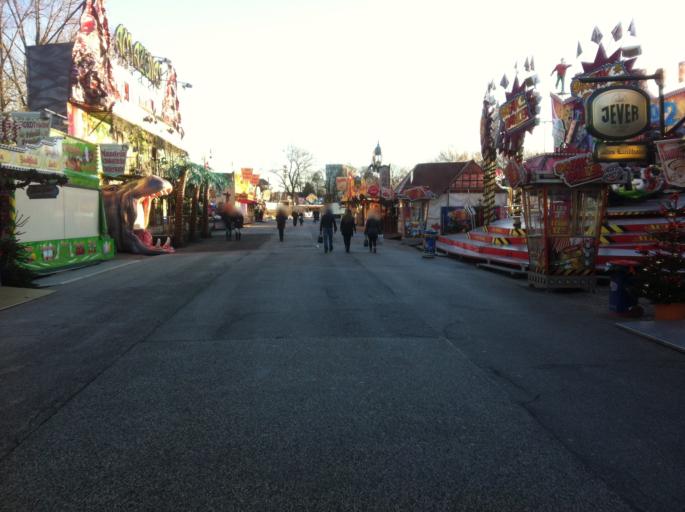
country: DE
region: Hamburg
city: St. Pauli
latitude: 53.5563
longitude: 9.9724
